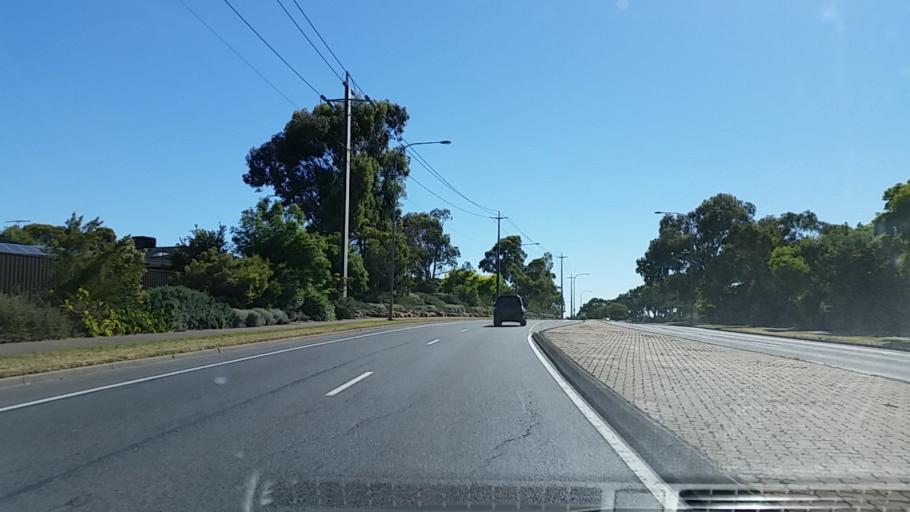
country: AU
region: South Australia
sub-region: Tea Tree Gully
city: Modbury
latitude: -34.8061
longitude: 138.6823
